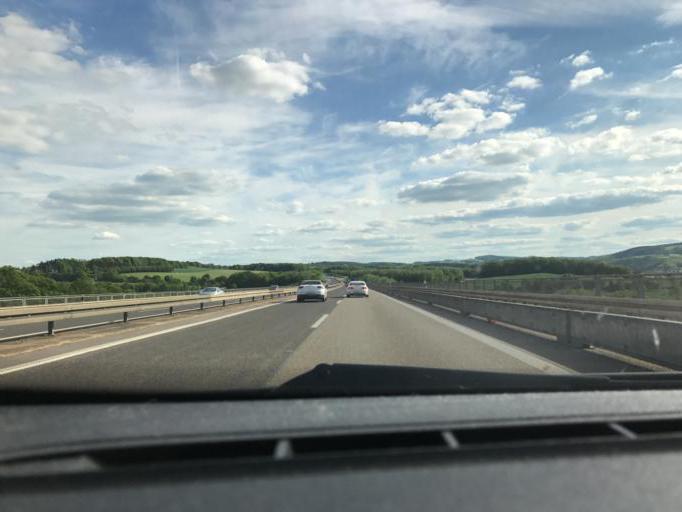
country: DE
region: North Rhine-Westphalia
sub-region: Regierungsbezirk Koln
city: Mechernich
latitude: 50.5802
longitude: 6.6898
